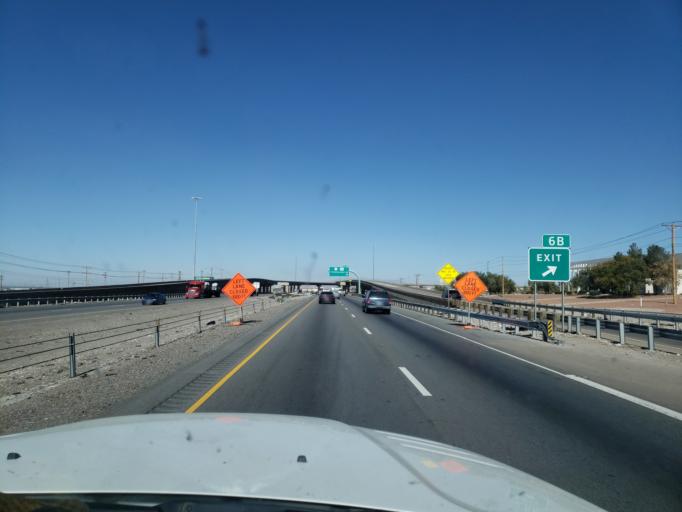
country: US
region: Texas
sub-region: El Paso County
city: Canutillo
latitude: 31.9010
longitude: -106.5827
